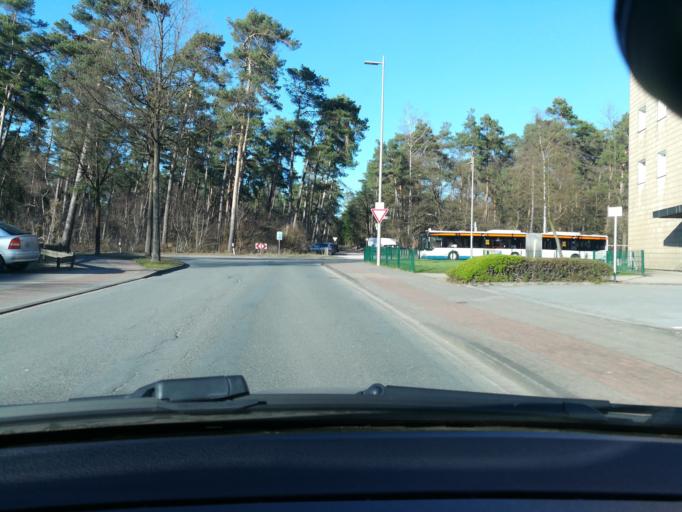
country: DE
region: North Rhine-Westphalia
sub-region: Regierungsbezirk Detmold
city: Oerlinghausen
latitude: 51.9562
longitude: 8.5985
